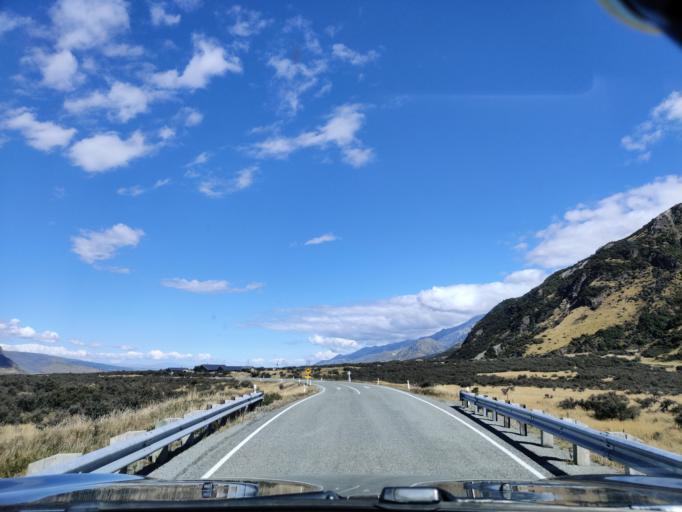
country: NZ
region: Canterbury
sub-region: Timaru District
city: Pleasant Point
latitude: -43.7553
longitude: 170.1175
